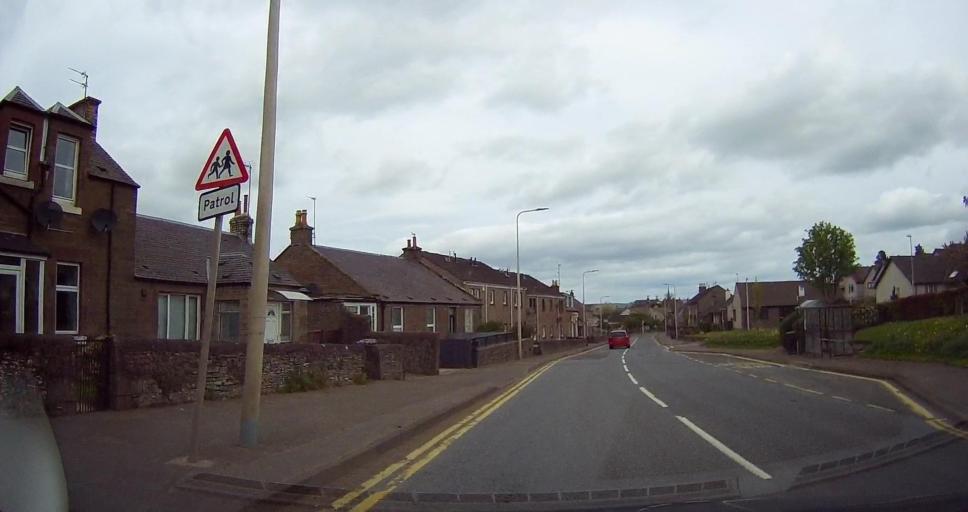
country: GB
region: Scotland
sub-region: Angus
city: Forfar
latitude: 56.6381
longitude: -2.8941
